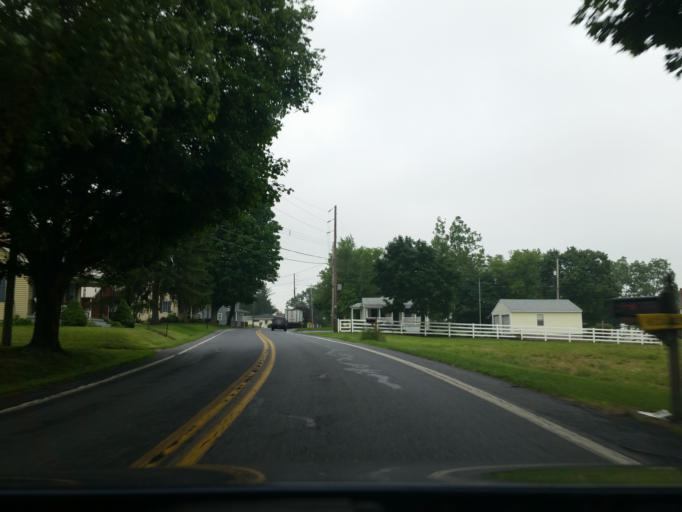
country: US
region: Pennsylvania
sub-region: Lebanon County
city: Jonestown
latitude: 40.3877
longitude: -76.5257
